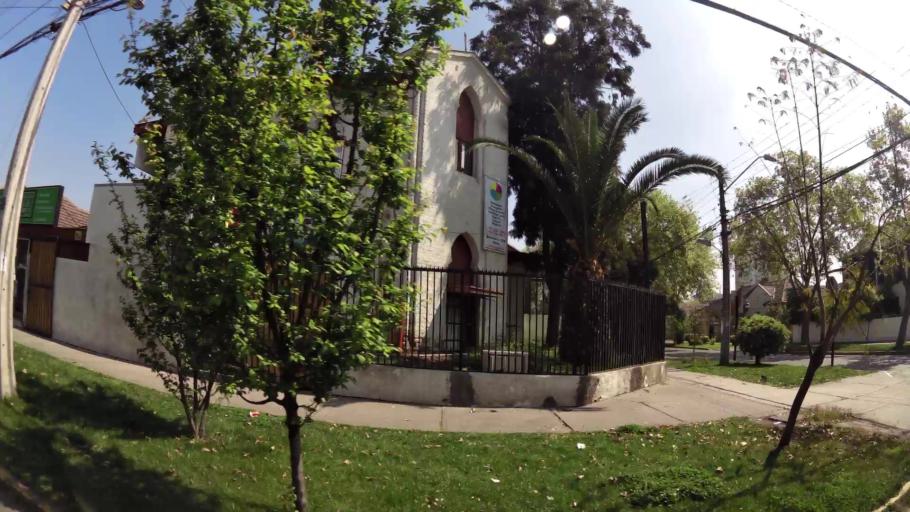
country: CL
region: Santiago Metropolitan
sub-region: Provincia de Santiago
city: Santiago
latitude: -33.4577
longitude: -70.6209
